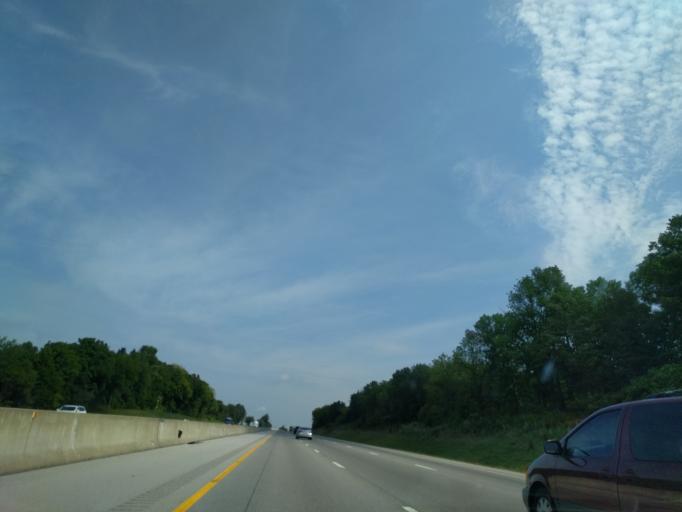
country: US
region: Kentucky
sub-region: Warren County
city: Plano
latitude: 36.8104
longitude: -86.4736
